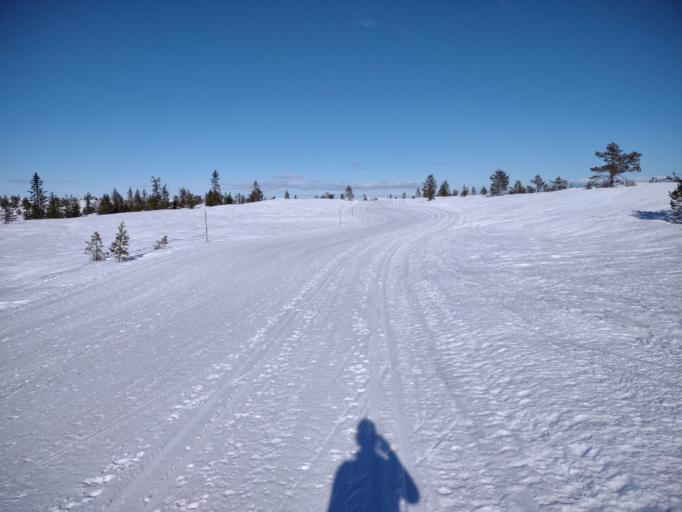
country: NO
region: Buskerud
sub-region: Flesberg
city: Lampeland
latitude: 59.7764
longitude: 9.3984
